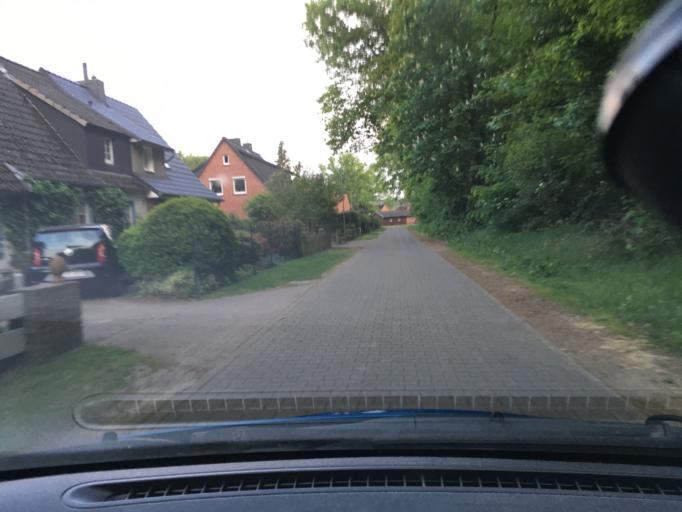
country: DE
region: Lower Saxony
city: Garstedt
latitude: 53.2845
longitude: 10.1589
